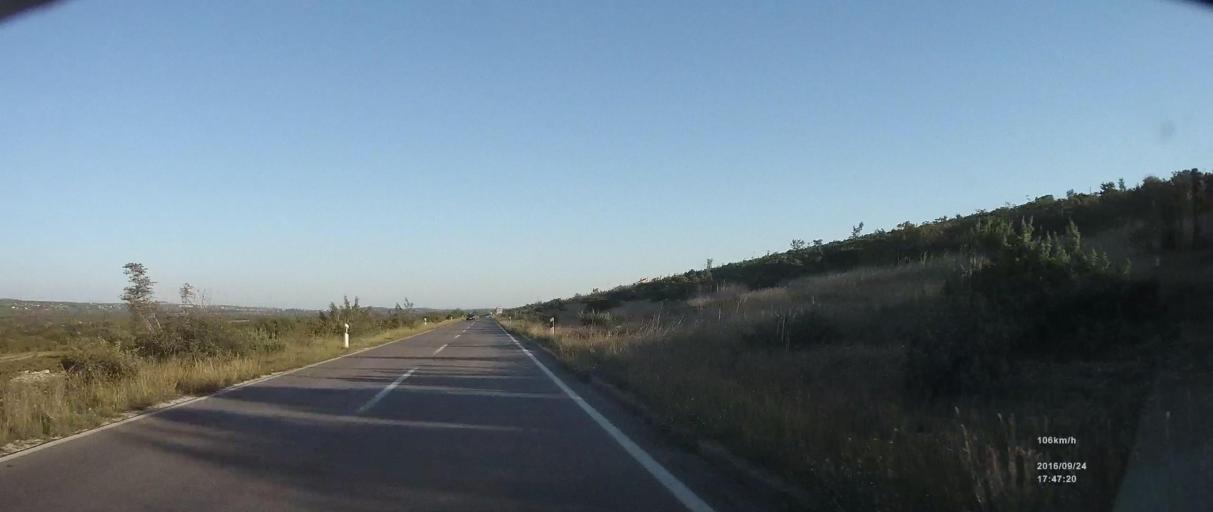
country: HR
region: Zadarska
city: Polaca
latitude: 44.0762
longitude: 15.5217
